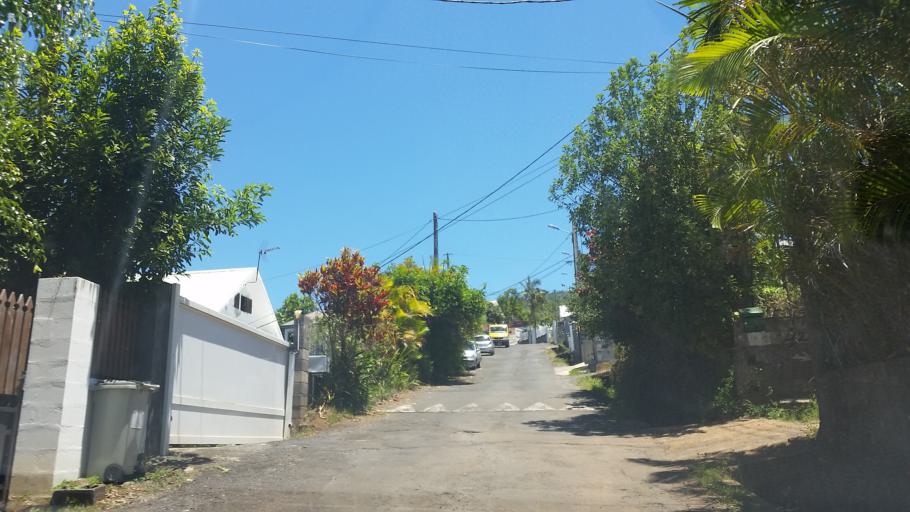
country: RE
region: Reunion
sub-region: Reunion
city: Sainte-Marie
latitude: -20.9326
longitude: 55.5313
